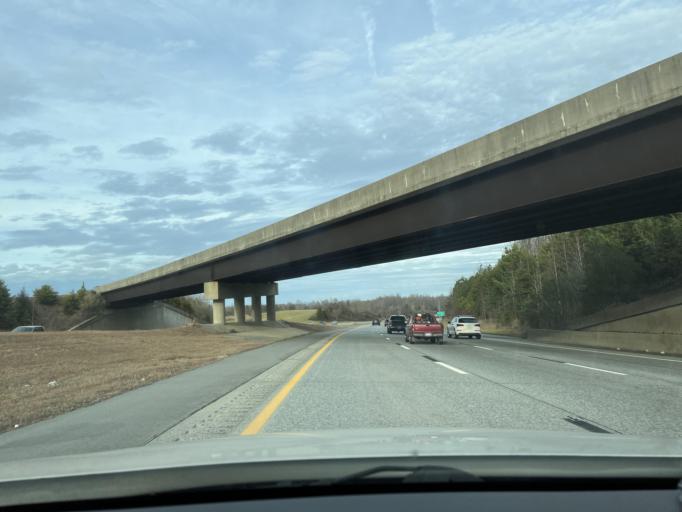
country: US
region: North Carolina
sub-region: Guilford County
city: McLeansville
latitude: 36.0547
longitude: -79.6845
